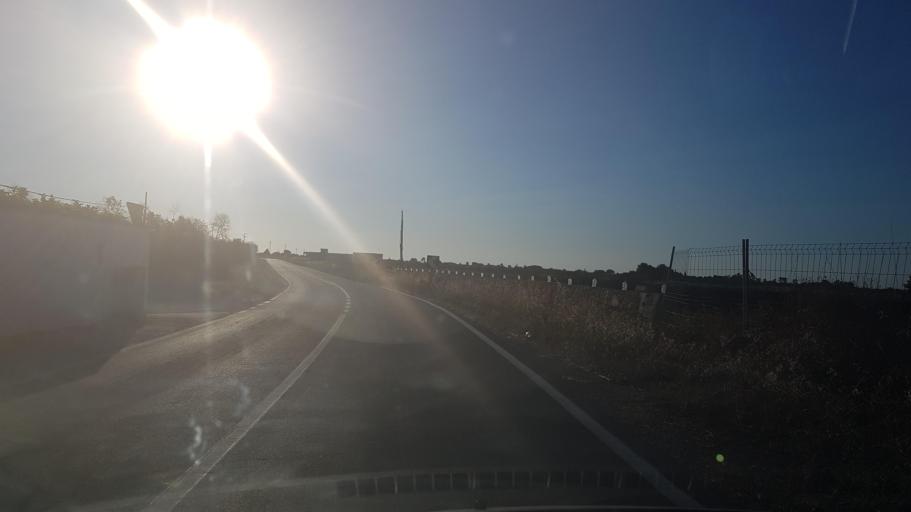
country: IT
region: Apulia
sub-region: Provincia di Lecce
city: Struda
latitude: 40.3283
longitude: 18.3099
